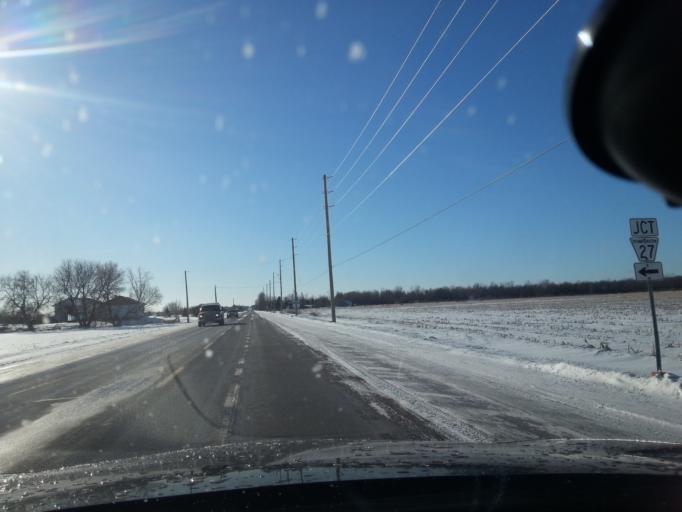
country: CA
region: Ontario
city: Ottawa
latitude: 45.3057
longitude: -75.5085
